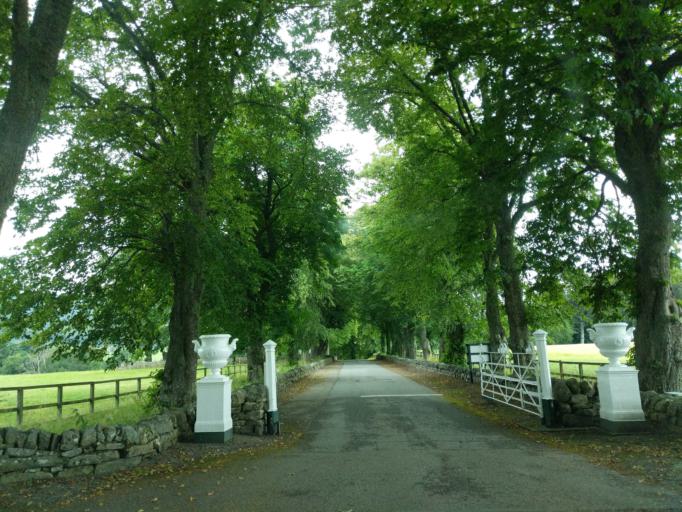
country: GB
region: Scotland
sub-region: Moray
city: Rothes
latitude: 57.4113
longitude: -3.3600
